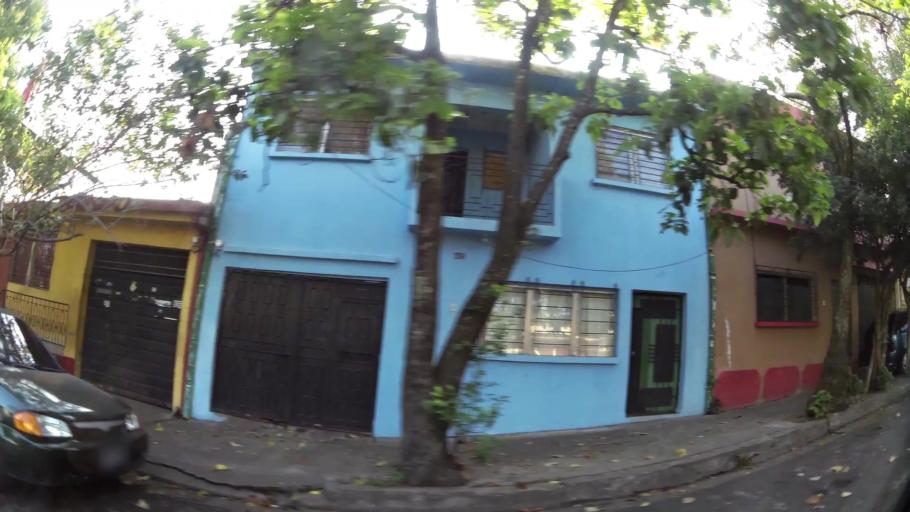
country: SV
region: San Salvador
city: San Salvador
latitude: 13.6789
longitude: -89.2006
